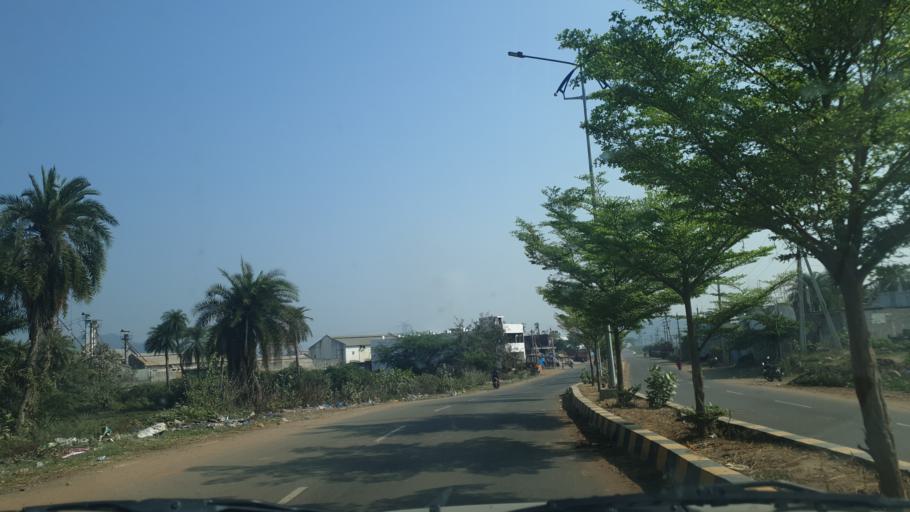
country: IN
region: Andhra Pradesh
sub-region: Srikakulam
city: Tekkali
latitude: 18.6133
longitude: 84.2357
